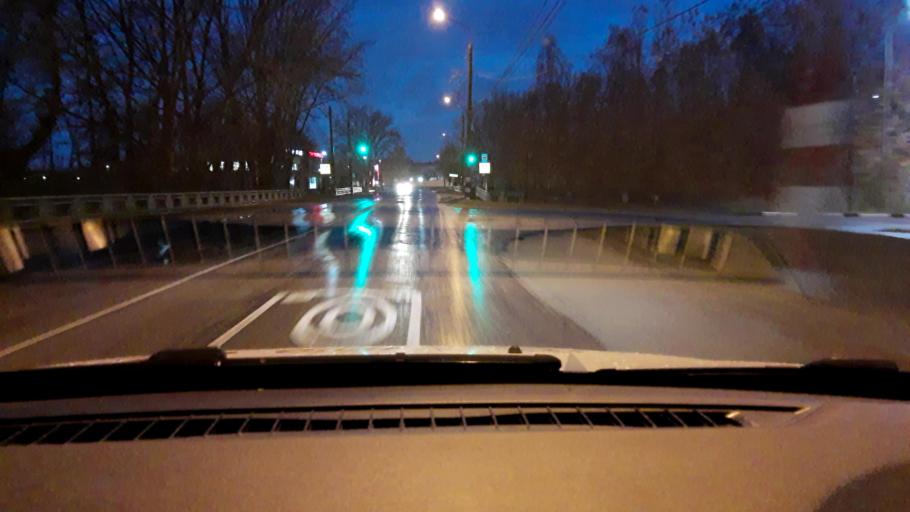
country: RU
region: Nizjnij Novgorod
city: Bor
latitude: 56.3430
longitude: 44.0903
